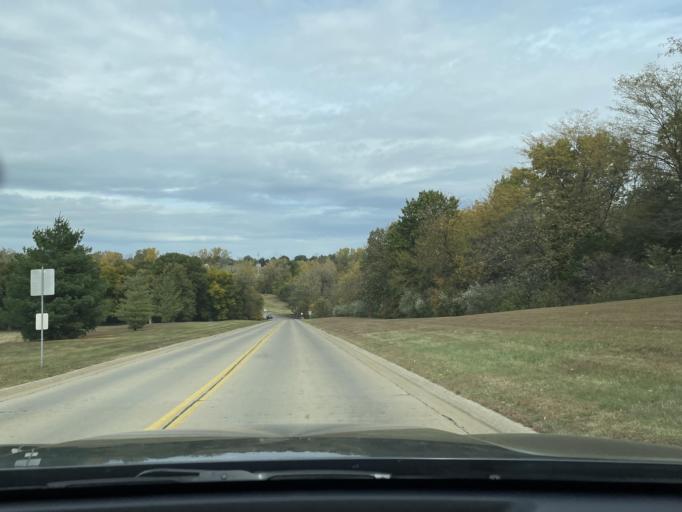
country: US
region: Missouri
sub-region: Buchanan County
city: Saint Joseph
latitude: 39.7628
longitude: -94.7813
